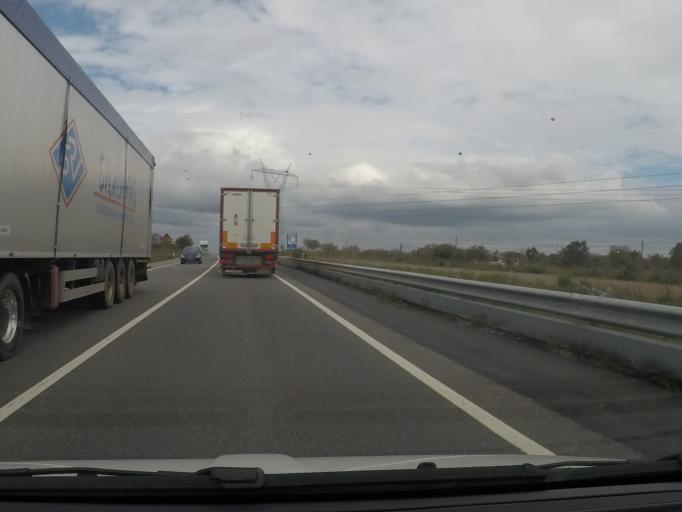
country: PT
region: Setubal
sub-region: Santiago do Cacem
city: Santiago do Cacem
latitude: 38.0713
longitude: -8.6563
